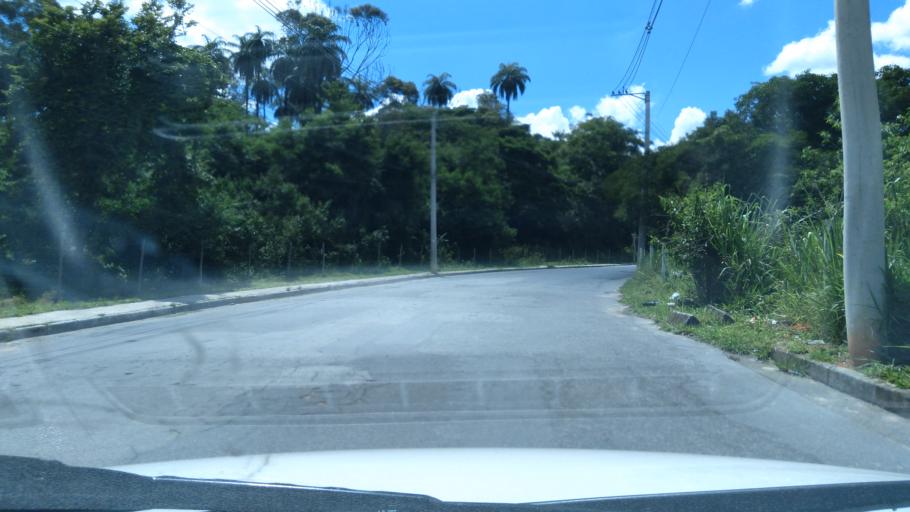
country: BR
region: Minas Gerais
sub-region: Santa Luzia
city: Santa Luzia
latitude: -19.8555
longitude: -43.8751
